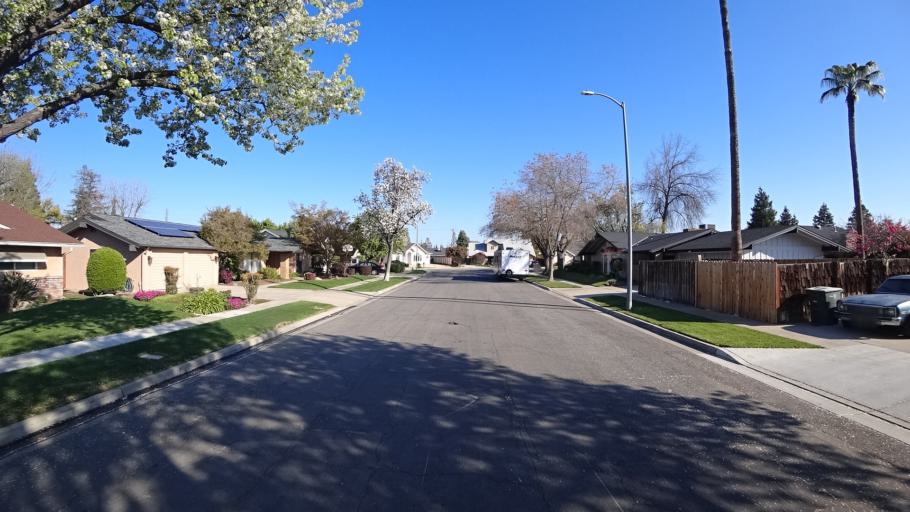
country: US
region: California
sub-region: Fresno County
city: Clovis
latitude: 36.8287
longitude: -119.7803
